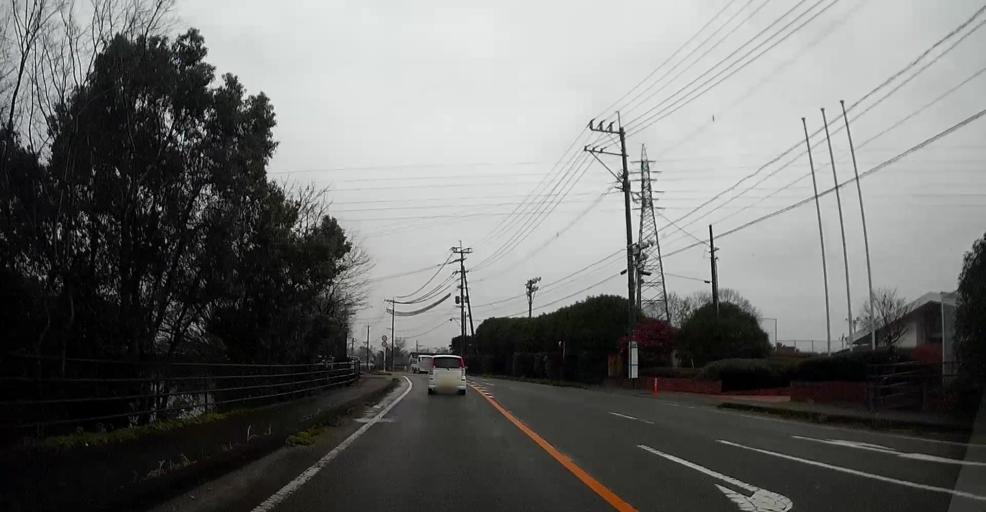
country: JP
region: Kumamoto
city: Kumamoto
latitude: 32.7638
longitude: 130.7528
